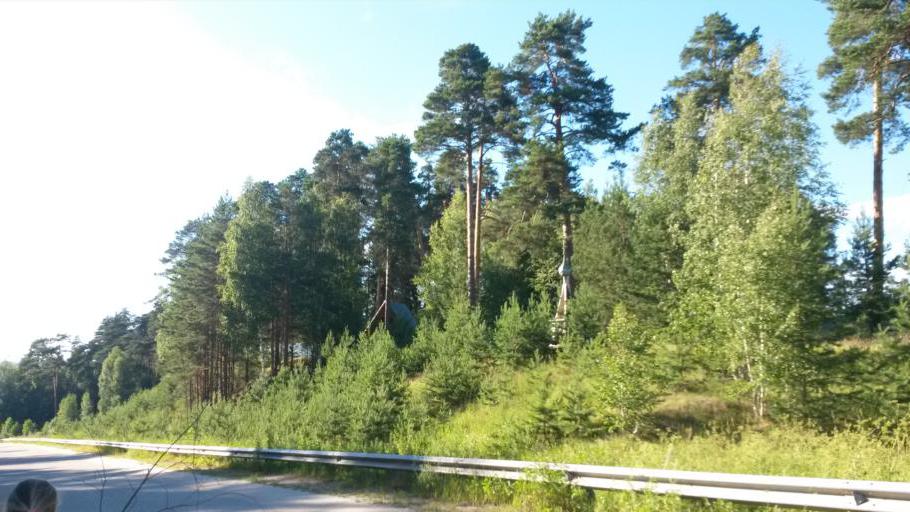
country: RU
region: Ivanovo
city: Zarechnyy
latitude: 57.5001
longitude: 42.3317
